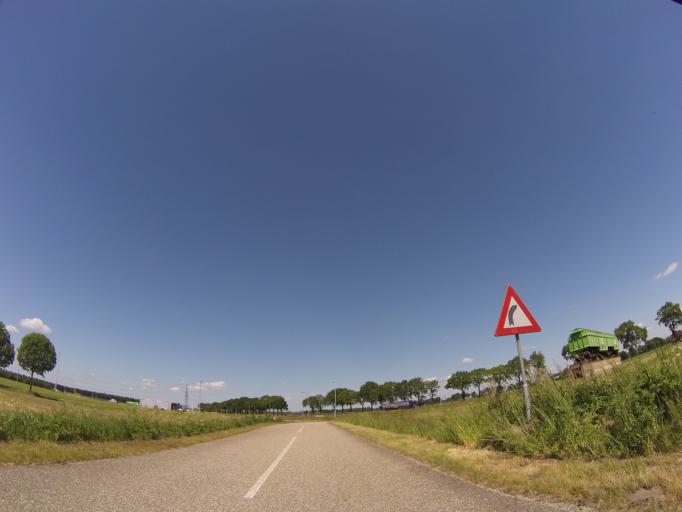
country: NL
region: Drenthe
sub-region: Gemeente Hoogeveen
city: Hoogeveen
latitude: 52.7899
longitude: 6.5064
